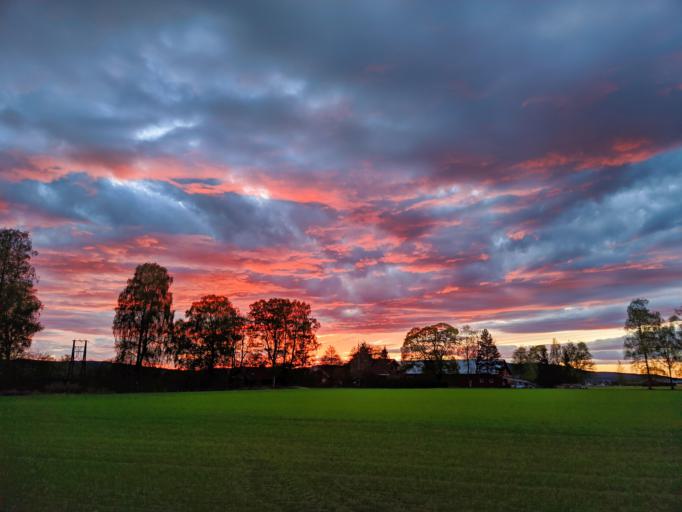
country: NO
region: Akershus
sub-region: Nannestad
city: Teigebyen
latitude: 60.2113
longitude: 11.0718
